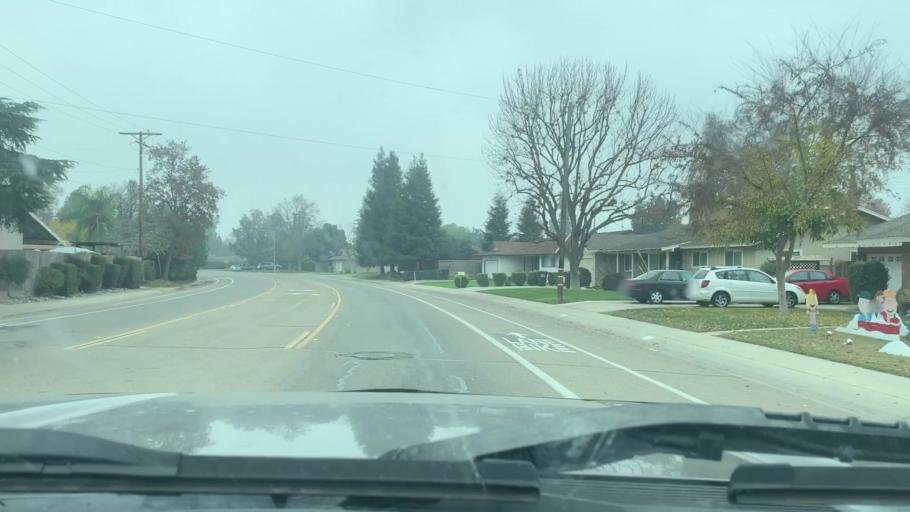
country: US
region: California
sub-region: Tulare County
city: Visalia
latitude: 36.3192
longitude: -119.3273
